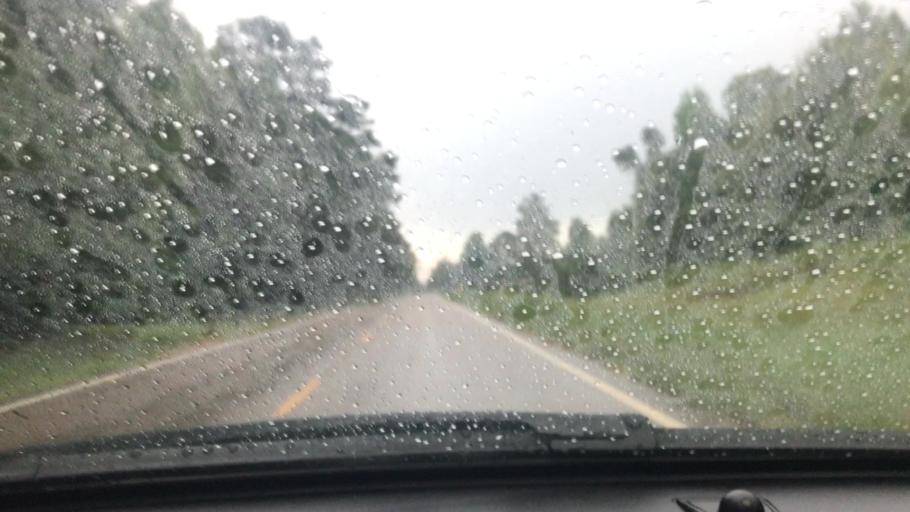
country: US
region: Mississippi
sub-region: Pike County
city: Summit
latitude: 31.2981
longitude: -90.5065
